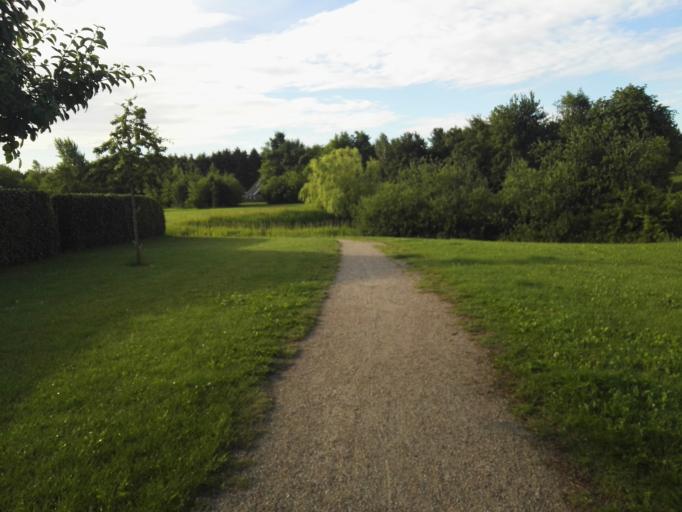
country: DK
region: Capital Region
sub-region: Egedal Kommune
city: Smorumnedre
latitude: 55.7414
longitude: 12.3157
